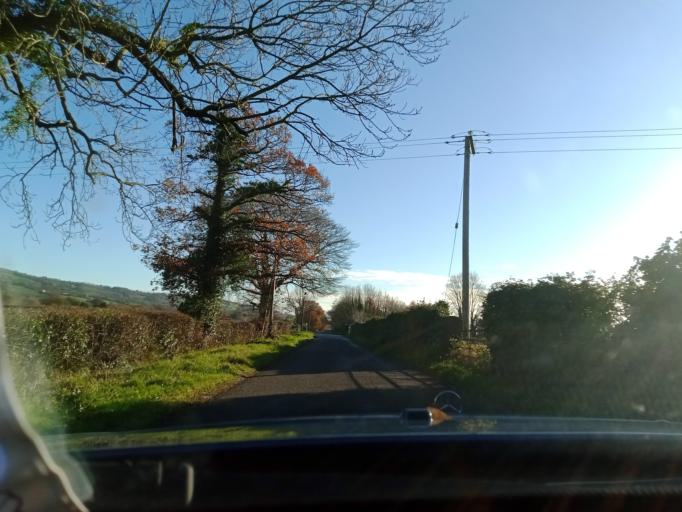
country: IE
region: Leinster
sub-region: Kilkenny
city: Piltown
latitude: 52.3607
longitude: -7.3107
